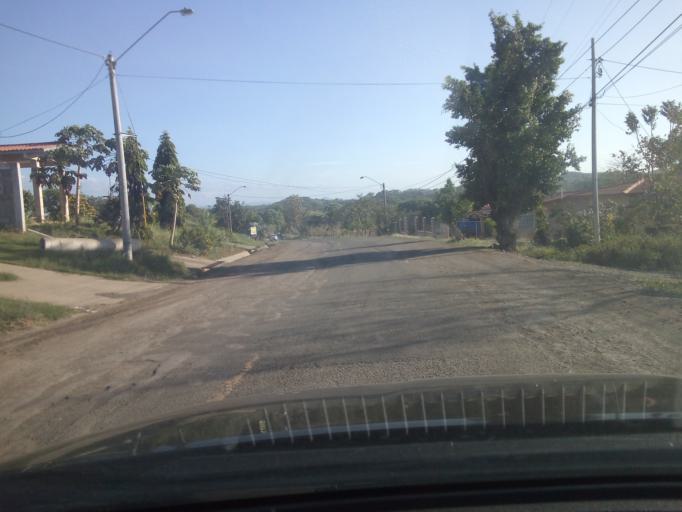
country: PA
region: Veraguas
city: Atalaya
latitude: 8.0442
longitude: -80.9321
